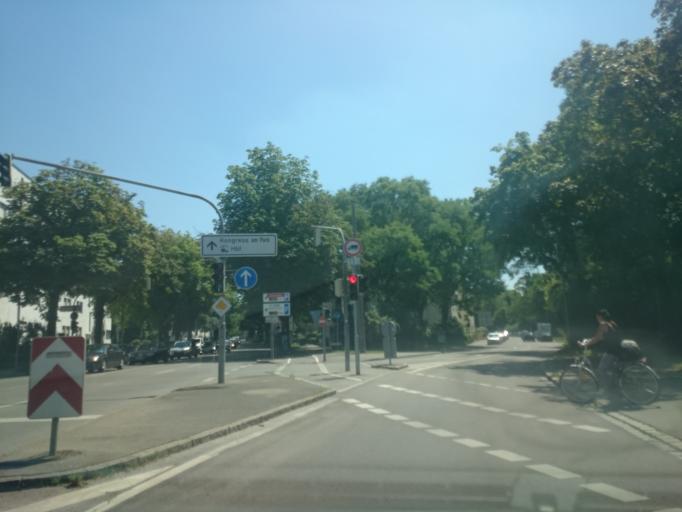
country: DE
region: Bavaria
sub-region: Swabia
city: Augsburg
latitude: 48.3692
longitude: 10.8787
